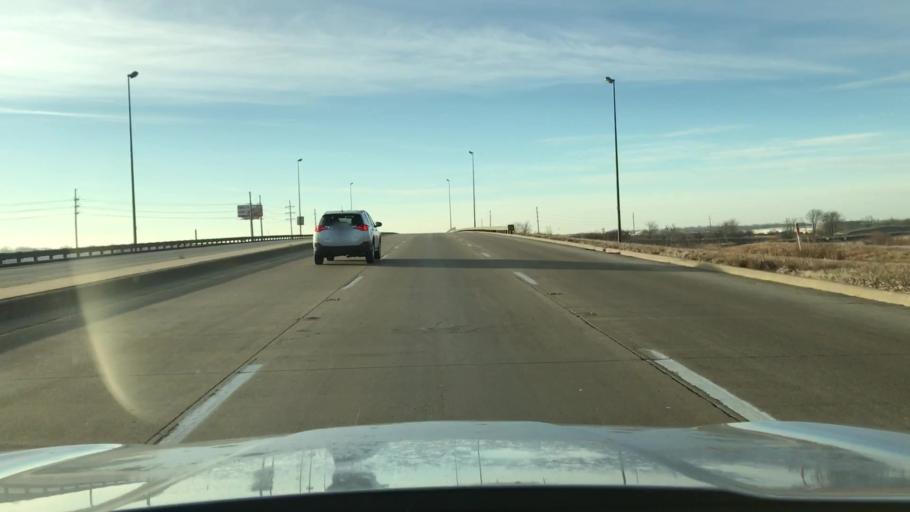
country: US
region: Illinois
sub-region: McLean County
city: Normal
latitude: 40.5316
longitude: -88.9516
